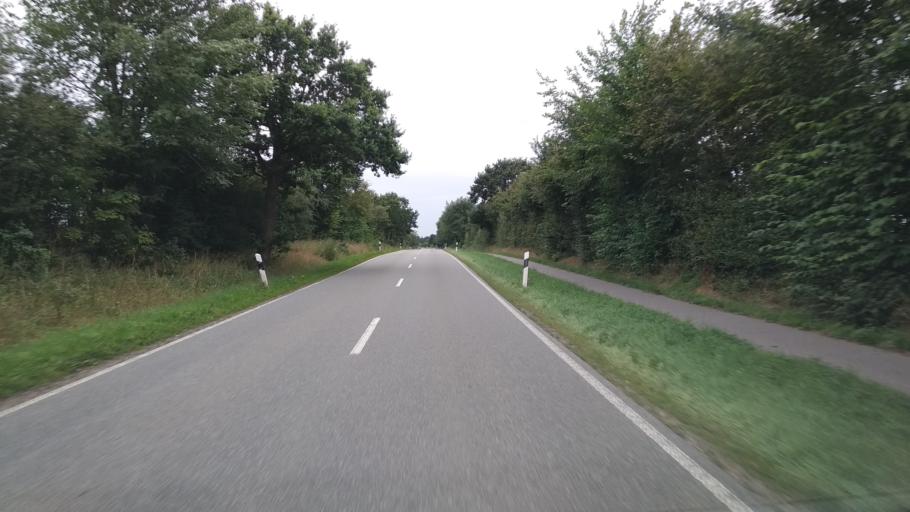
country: DE
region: Schleswig-Holstein
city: Lurschau
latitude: 54.5339
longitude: 9.4907
